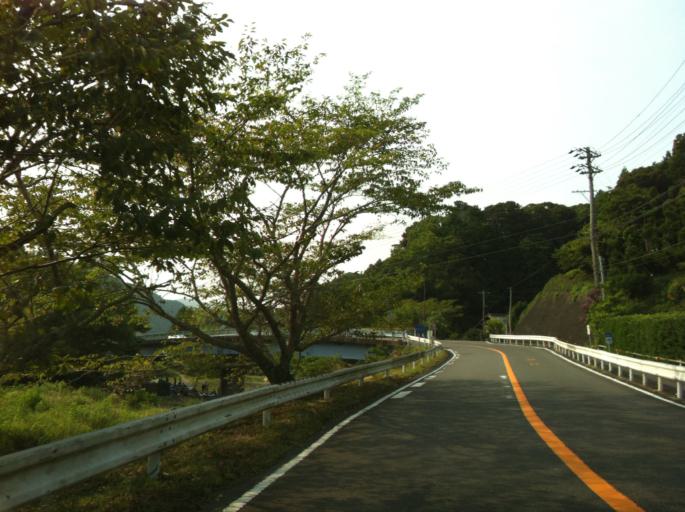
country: JP
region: Shizuoka
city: Fujieda
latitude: 34.9299
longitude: 138.2700
